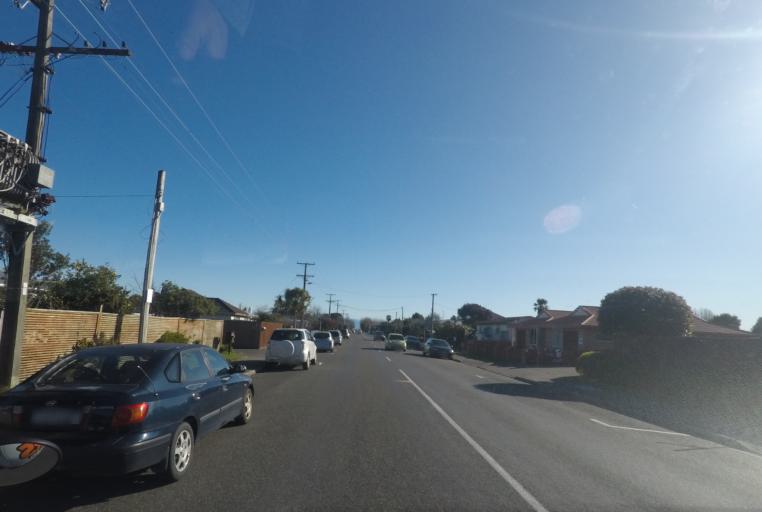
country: NZ
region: Nelson
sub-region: Nelson City
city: Nelson
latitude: -41.2879
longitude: 173.2377
